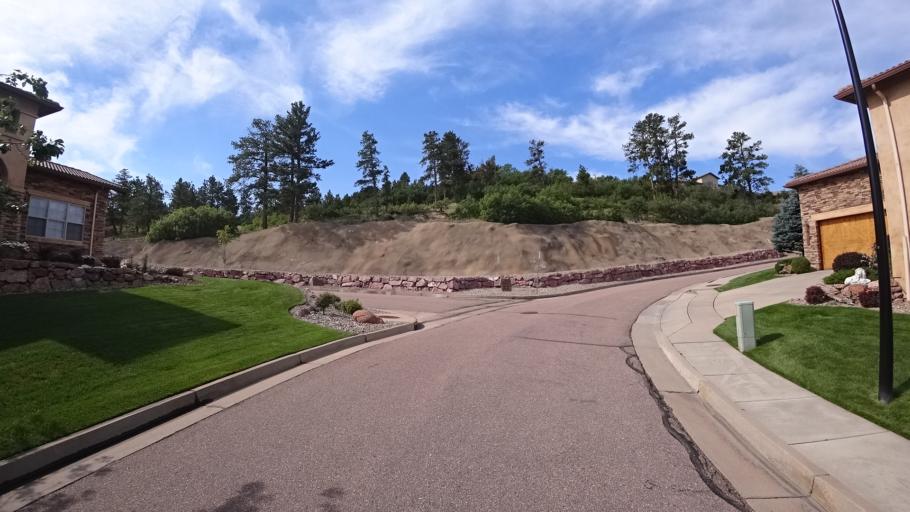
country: US
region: Colorado
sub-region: El Paso County
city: Air Force Academy
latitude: 38.9422
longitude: -104.8597
